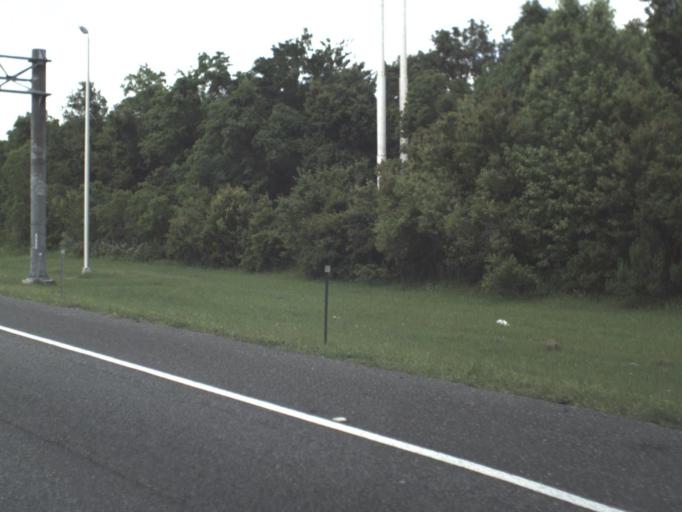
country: US
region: Florida
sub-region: Saint Johns County
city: Saint Augustine
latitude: 29.9128
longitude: -81.4104
